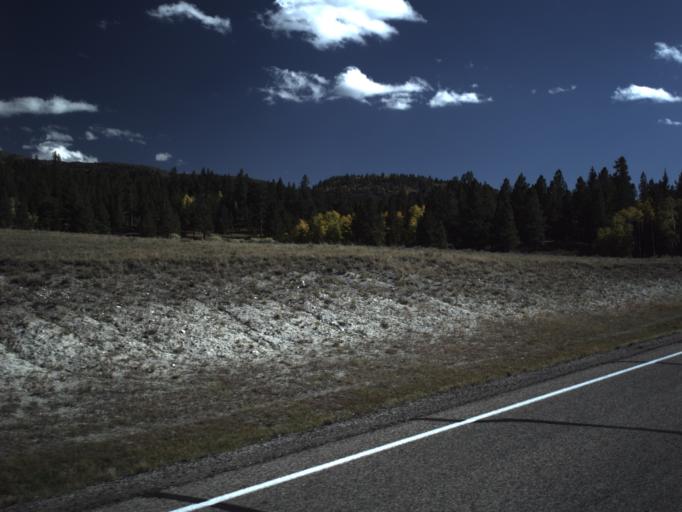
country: US
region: Utah
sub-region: Iron County
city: Parowan
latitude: 37.6856
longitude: -112.6649
